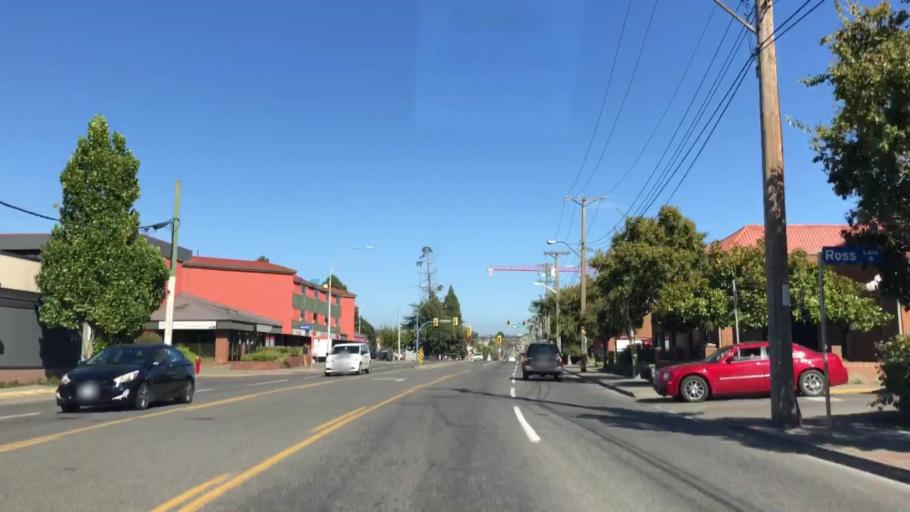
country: CA
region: British Columbia
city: Victoria
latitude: 48.4386
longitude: -123.3653
